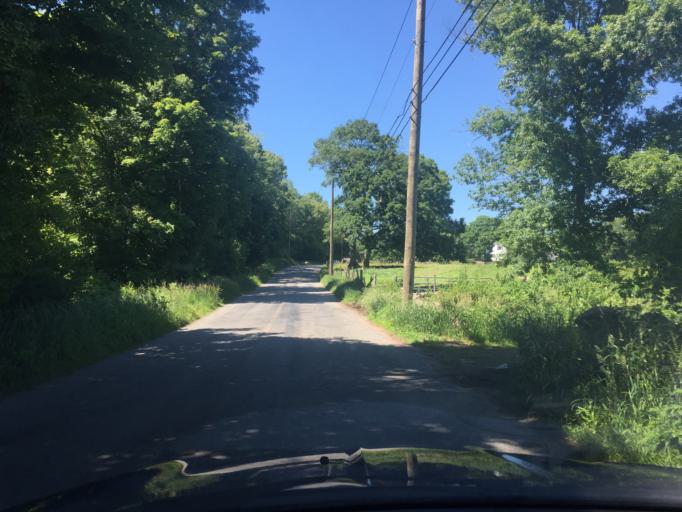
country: US
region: Rhode Island
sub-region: Washington County
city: Hopkinton
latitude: 41.4586
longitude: -71.8150
